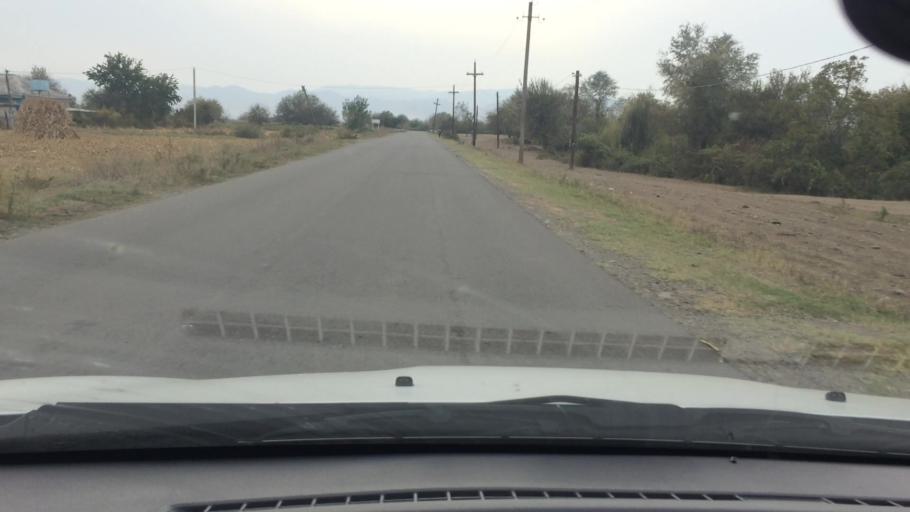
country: AM
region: Tavush
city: Bagratashen
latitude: 41.3399
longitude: 44.8834
